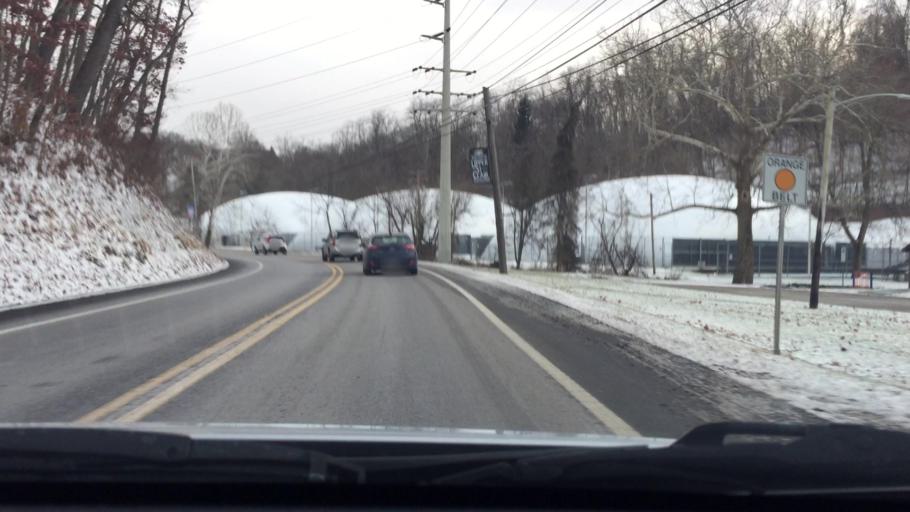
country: US
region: Pennsylvania
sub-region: Allegheny County
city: Upper Saint Clair
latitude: 40.3400
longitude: -80.0781
